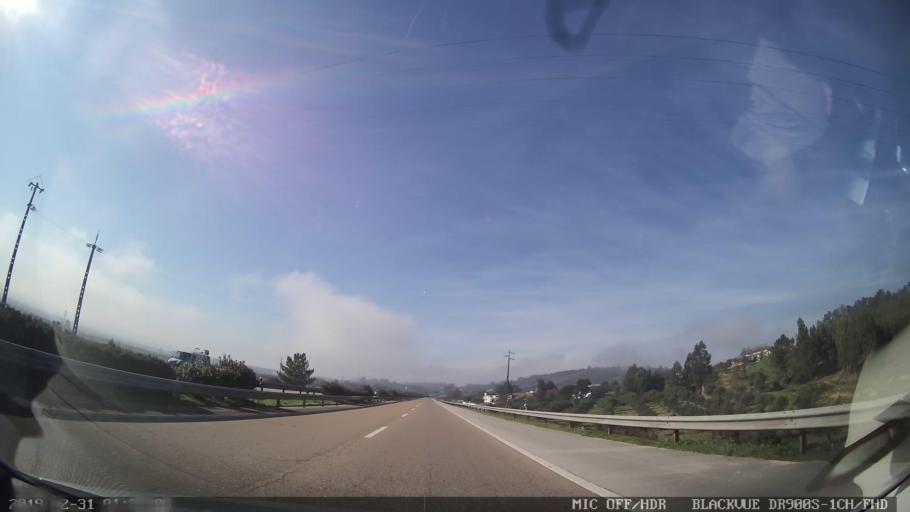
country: PT
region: Santarem
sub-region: Abrantes
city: Tramagal
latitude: 39.4869
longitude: -8.2644
